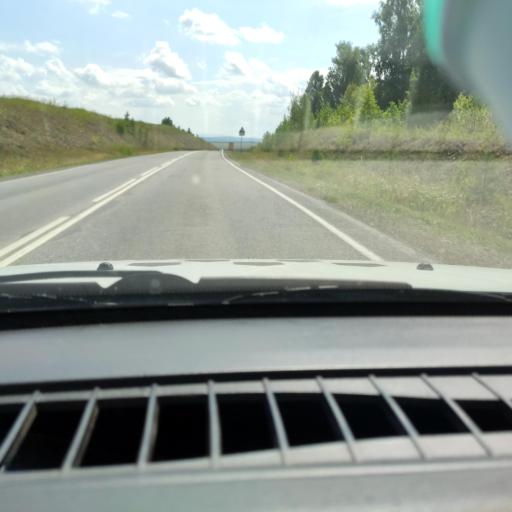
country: RU
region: Bashkortostan
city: Verkhniye Kigi
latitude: 55.3422
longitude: 58.6856
